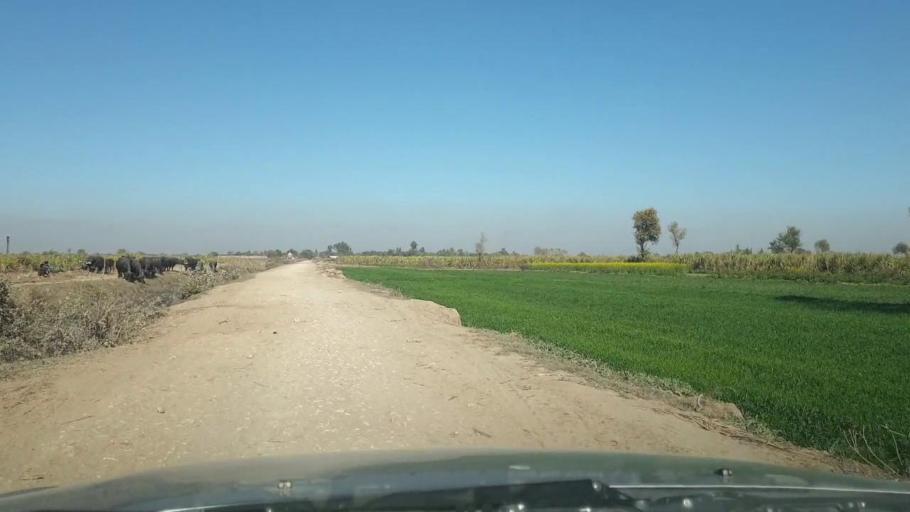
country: PK
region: Sindh
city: Ghotki
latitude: 28.0358
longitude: 69.2464
